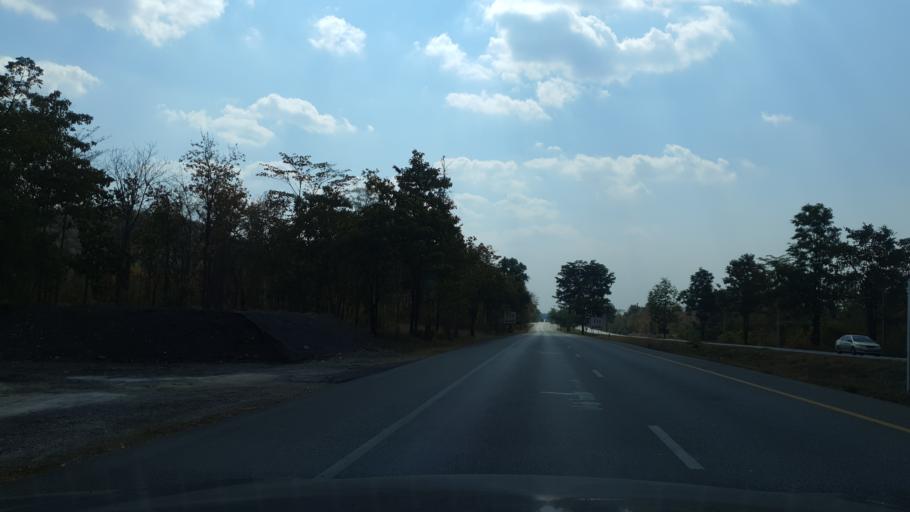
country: TH
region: Lampang
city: Mae Phrik
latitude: 17.3281
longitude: 99.1533
